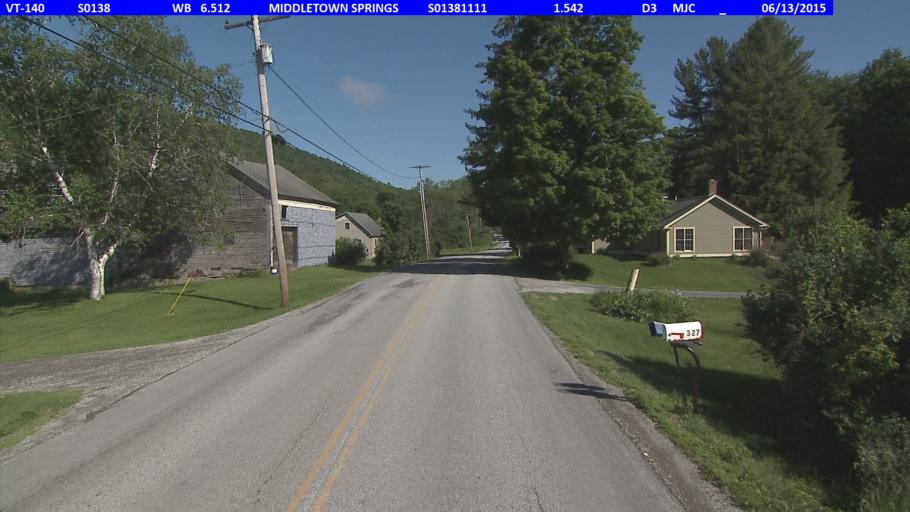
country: US
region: Vermont
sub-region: Rutland County
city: Poultney
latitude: 43.4853
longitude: -73.1501
